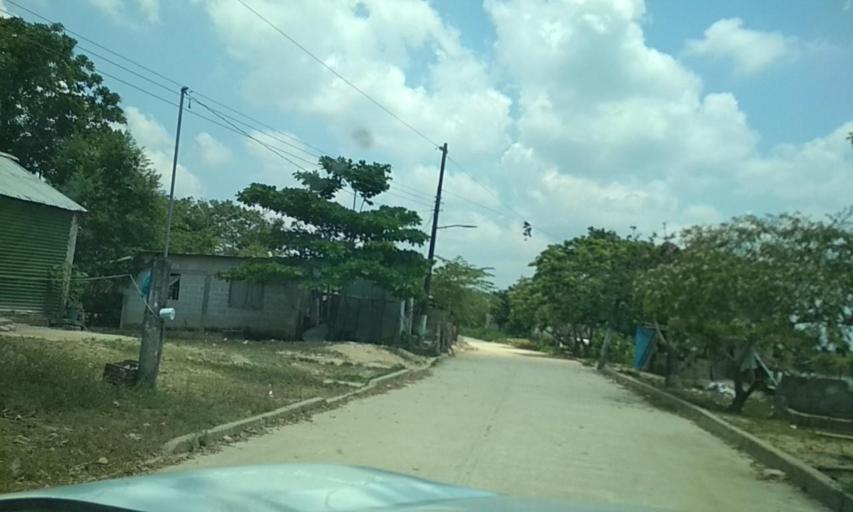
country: MX
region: Veracruz
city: Las Choapas
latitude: 17.9152
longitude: -94.0851
